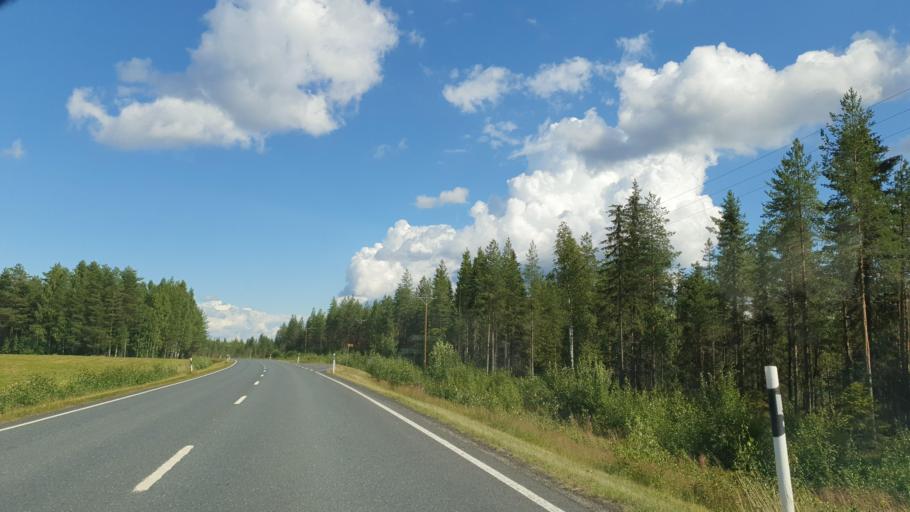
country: FI
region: Kainuu
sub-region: Kehys-Kainuu
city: Kuhmo
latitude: 64.0839
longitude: 29.0596
